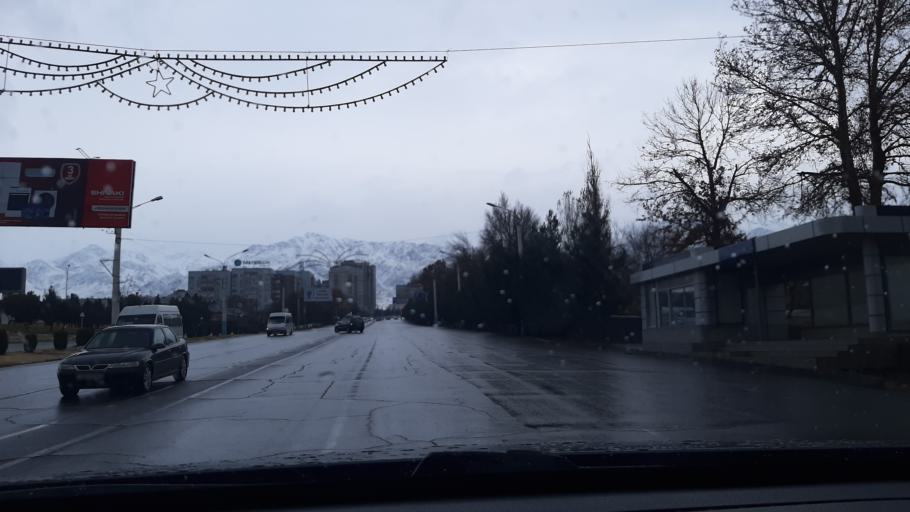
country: TJ
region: Viloyati Sughd
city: Khujand
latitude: 40.2949
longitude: 69.6175
